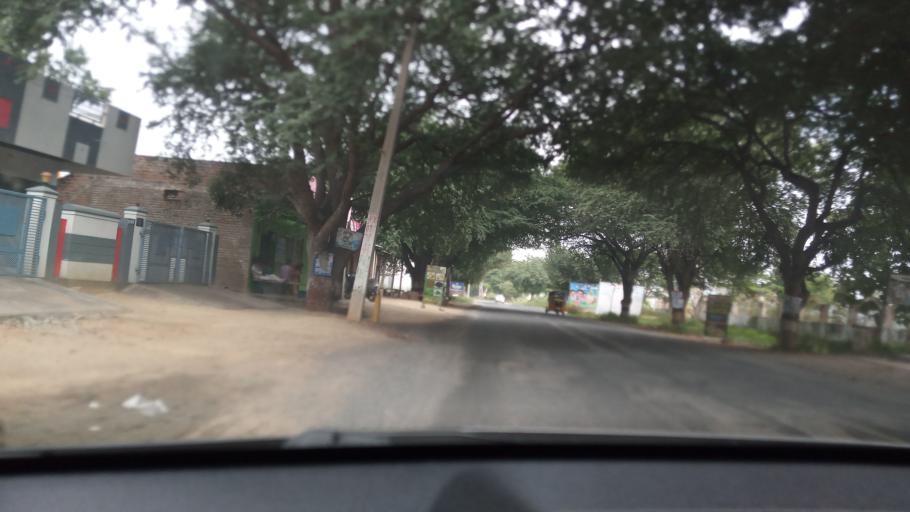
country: IN
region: Andhra Pradesh
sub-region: Chittoor
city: Madanapalle
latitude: 13.6517
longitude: 78.8167
